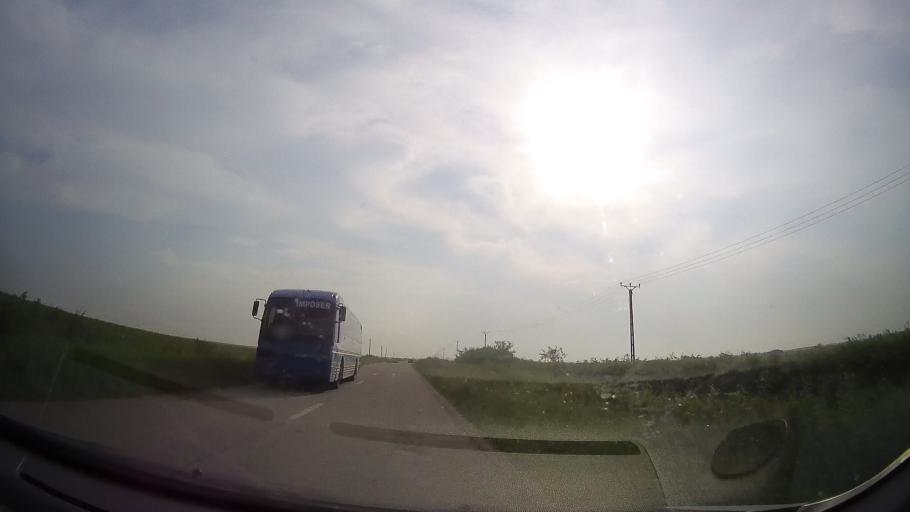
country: RO
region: Timis
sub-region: Comuna Foeni
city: Foeni
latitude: 45.5257
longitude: 20.9269
